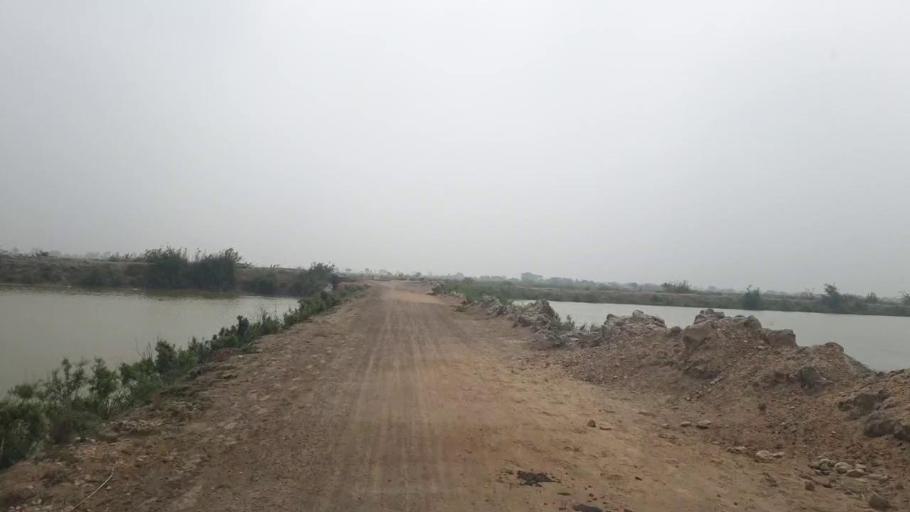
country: PK
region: Sindh
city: Badin
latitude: 24.5785
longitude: 68.6834
